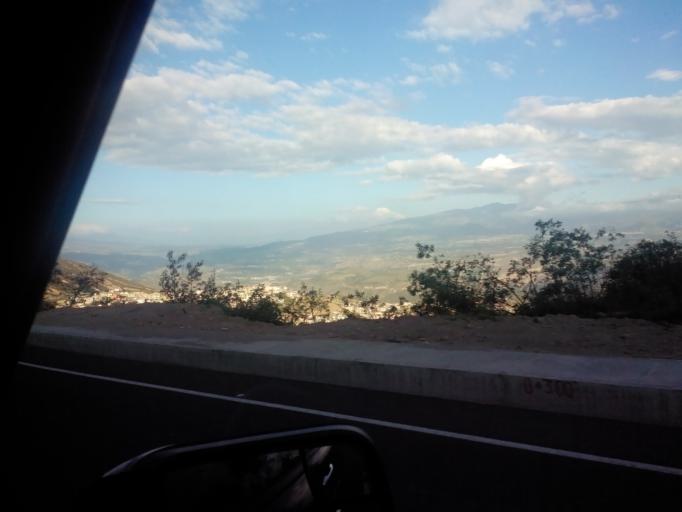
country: EC
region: Pichincha
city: Quito
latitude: -0.0984
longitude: -78.4189
